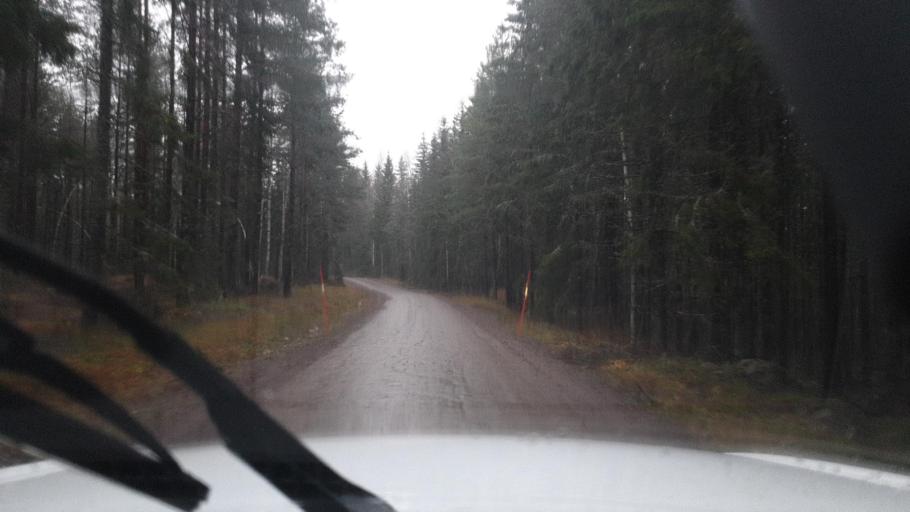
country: SE
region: Vaermland
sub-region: Arvika Kommun
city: Arvika
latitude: 59.9670
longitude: 12.6598
